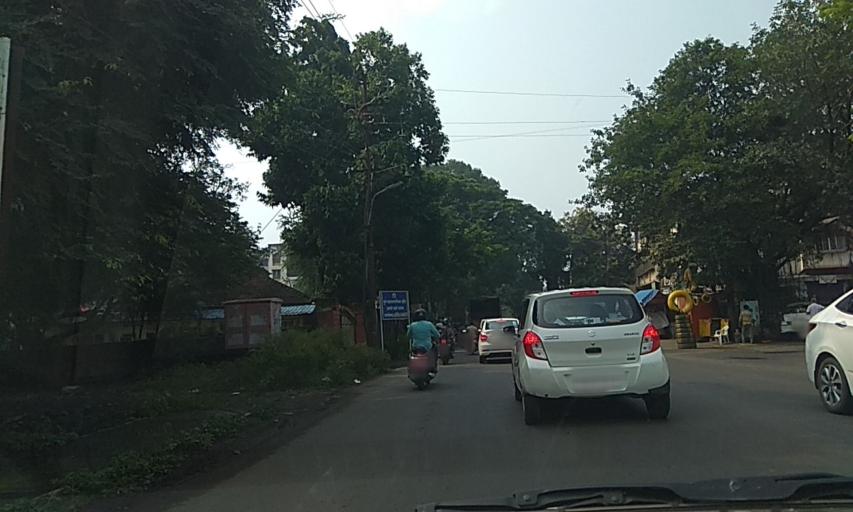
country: IN
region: Maharashtra
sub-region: Pune Division
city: Khadki
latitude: 18.5514
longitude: 73.8560
